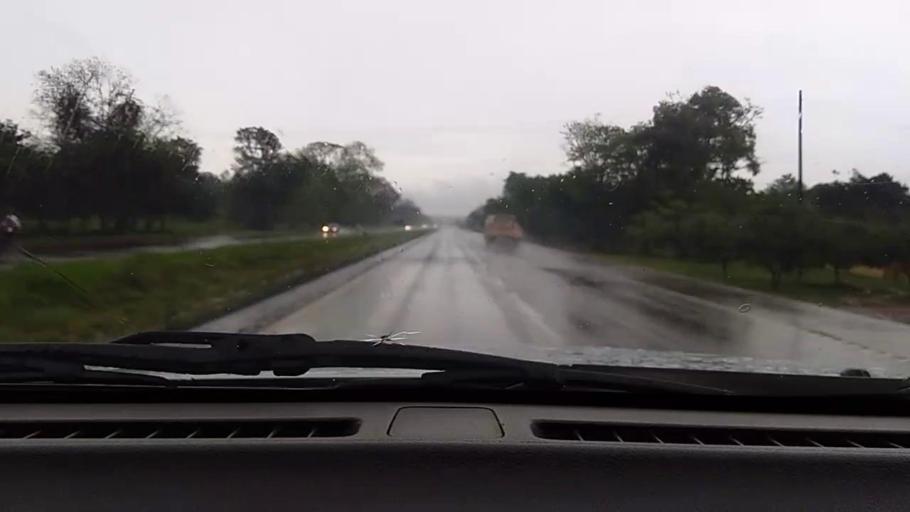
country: PY
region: Caaguazu
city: Repatriacion
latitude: -25.4571
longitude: -55.9172
